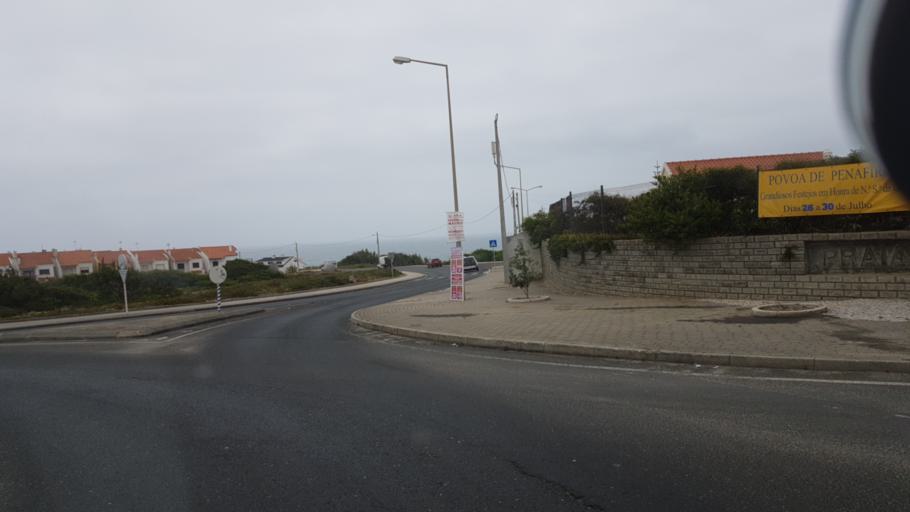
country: PT
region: Lisbon
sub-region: Torres Vedras
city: Silveira
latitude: 39.1439
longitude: -9.3707
